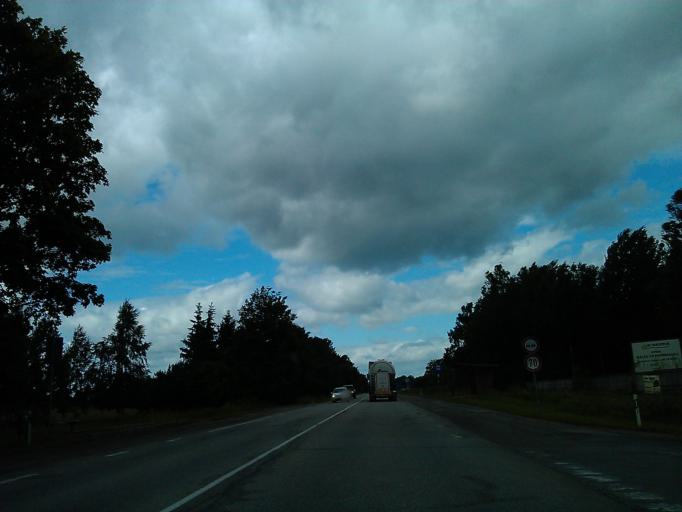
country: LV
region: Tukuma Rajons
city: Tukums
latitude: 56.9307
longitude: 23.2111
